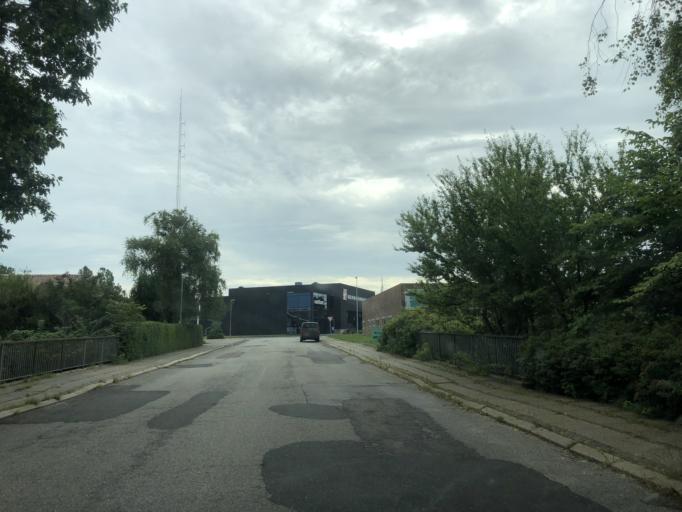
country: DK
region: Central Jutland
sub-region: Holstebro Kommune
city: Holstebro
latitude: 56.3796
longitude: 8.6111
